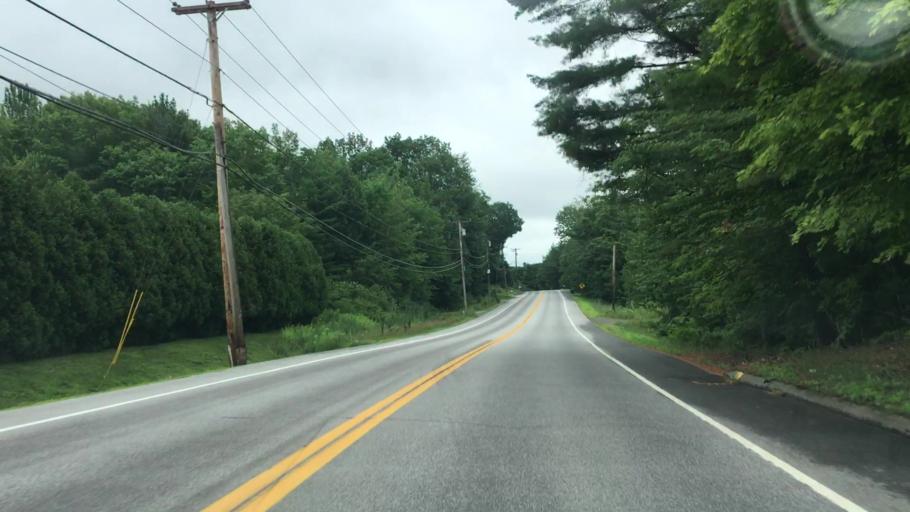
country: US
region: Maine
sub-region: Kennebec County
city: Chelsea
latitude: 44.2972
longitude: -69.7255
